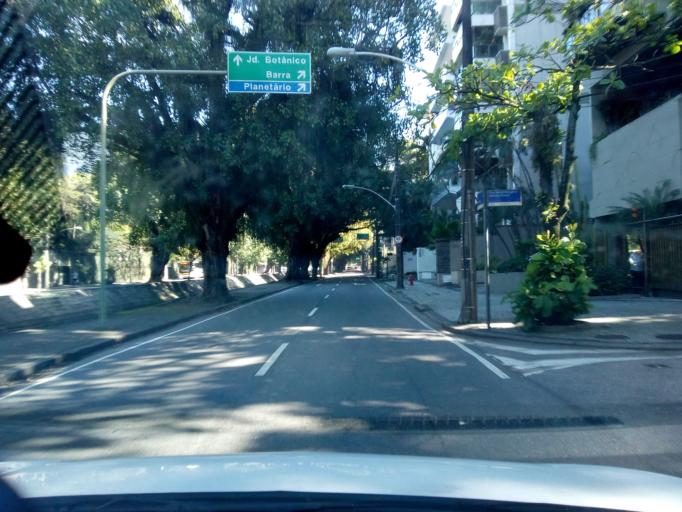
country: BR
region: Rio de Janeiro
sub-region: Rio De Janeiro
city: Rio de Janeiro
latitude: -22.9815
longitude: -43.2265
